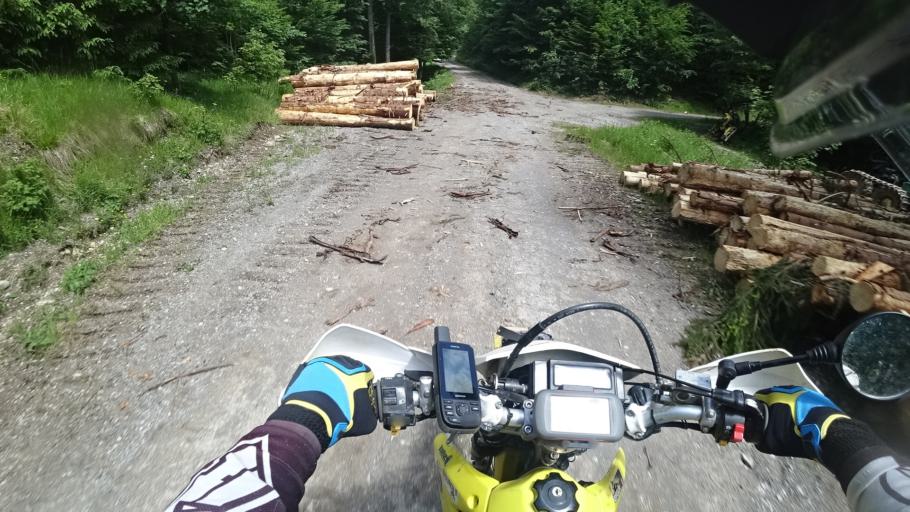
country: SI
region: Loska Dolina
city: Leskova Dolina
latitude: 45.5921
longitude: 14.5616
